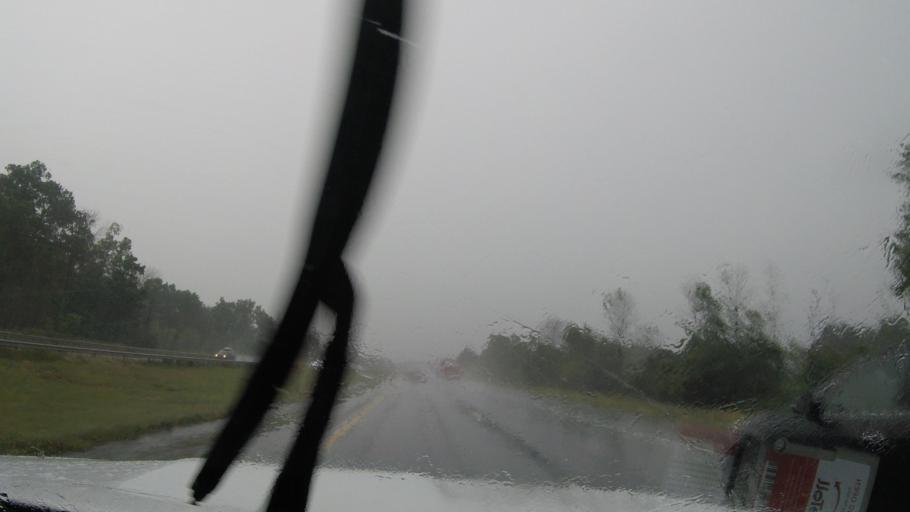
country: US
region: New York
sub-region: Seneca County
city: Seneca Falls
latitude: 42.9685
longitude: -76.8350
